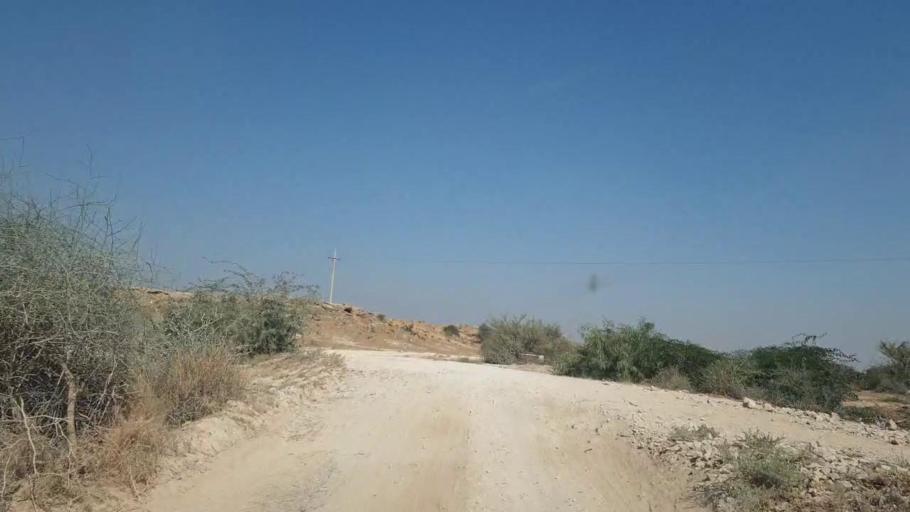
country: PK
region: Sindh
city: Thatta
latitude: 25.2177
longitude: 67.7959
